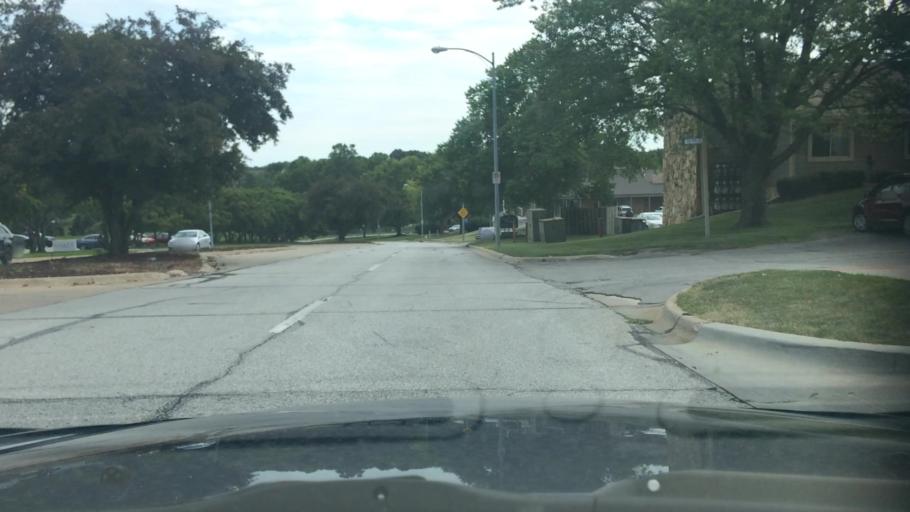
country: US
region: Nebraska
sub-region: Douglas County
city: Ralston
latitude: 41.2047
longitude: -96.0676
